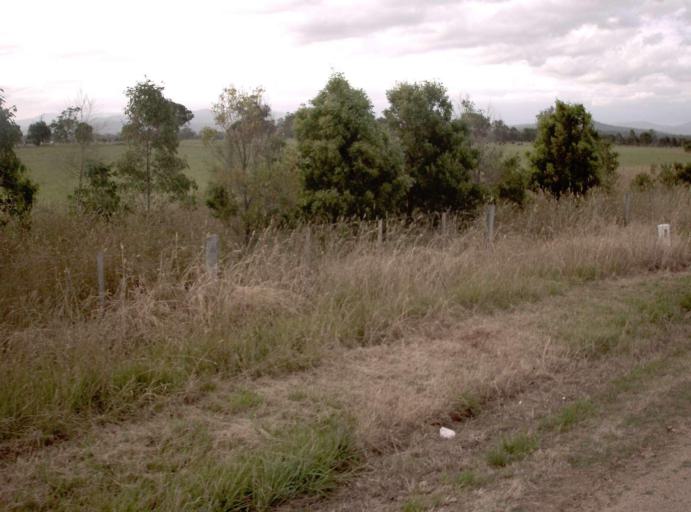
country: AU
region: Victoria
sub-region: Wellington
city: Sale
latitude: -37.8480
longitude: 147.0546
